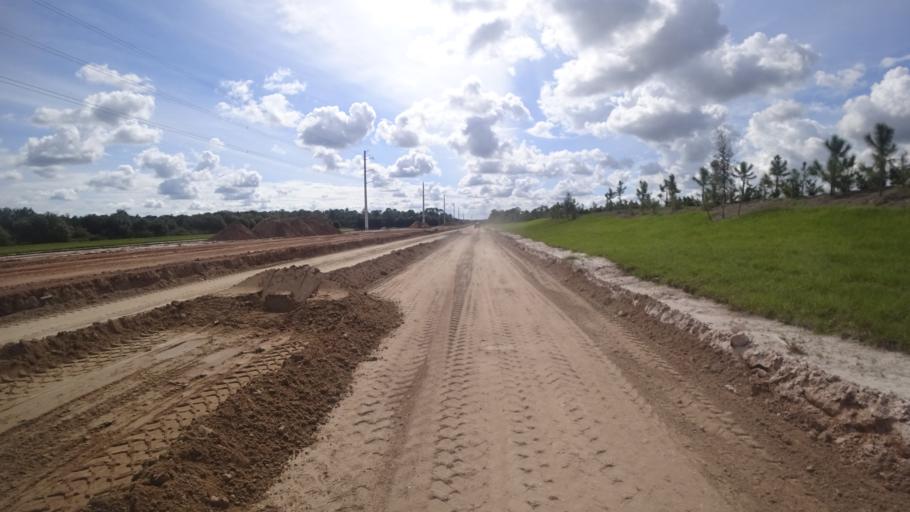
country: US
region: Florida
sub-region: Sarasota County
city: The Meadows
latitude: 27.4308
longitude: -82.3522
